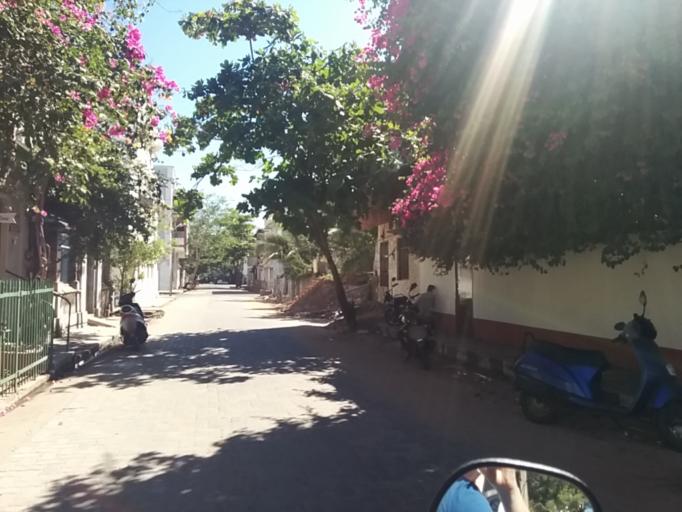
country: IN
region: Pondicherry
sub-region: Puducherry
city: Puducherry
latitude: 11.9390
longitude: 79.8352
